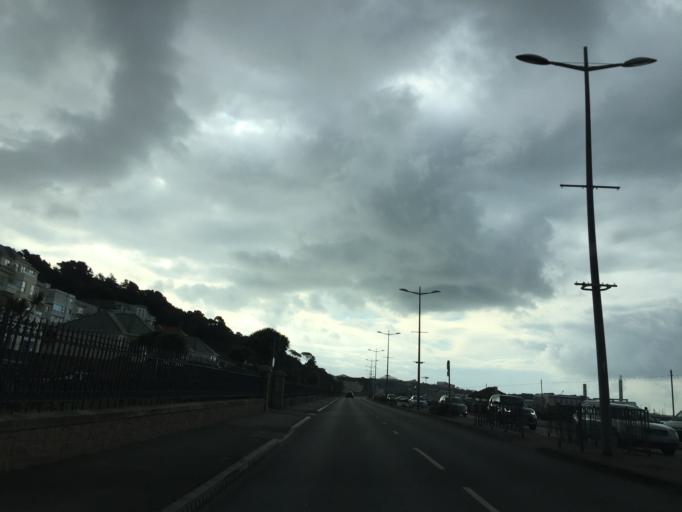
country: JE
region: St Helier
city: Saint Helier
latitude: 49.1920
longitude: -2.1243
